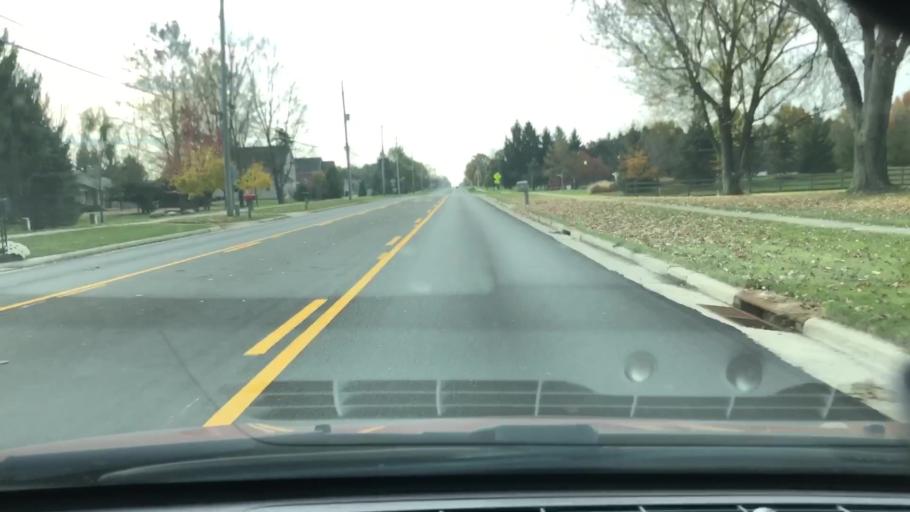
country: US
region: Ohio
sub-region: Franklin County
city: Westerville
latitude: 40.1666
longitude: -82.8996
